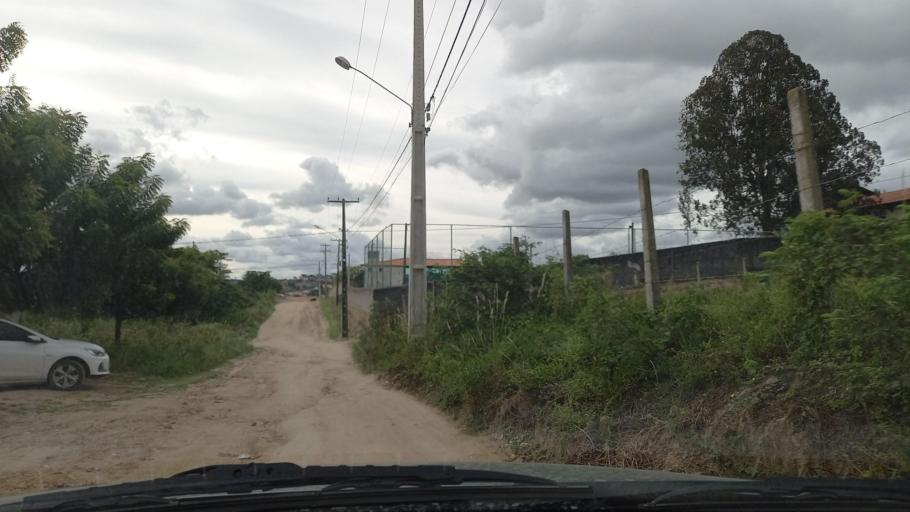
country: BR
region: Pernambuco
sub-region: Gravata
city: Gravata
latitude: -8.2025
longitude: -35.5455
